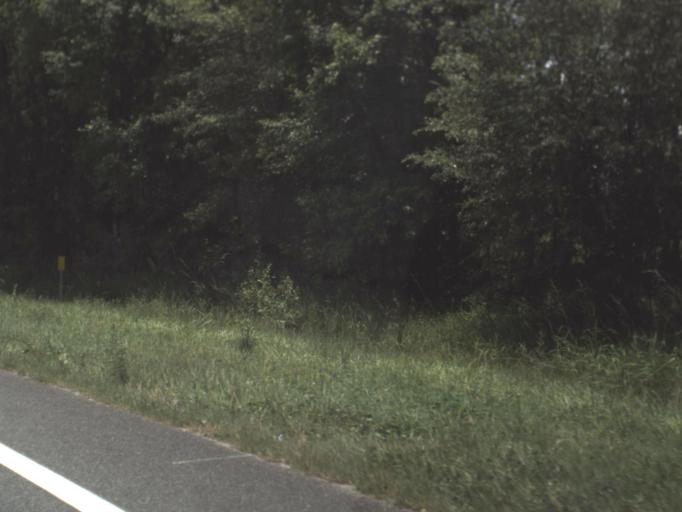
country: US
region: Florida
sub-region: Columbia County
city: Five Points
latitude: 30.2358
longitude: -82.6681
